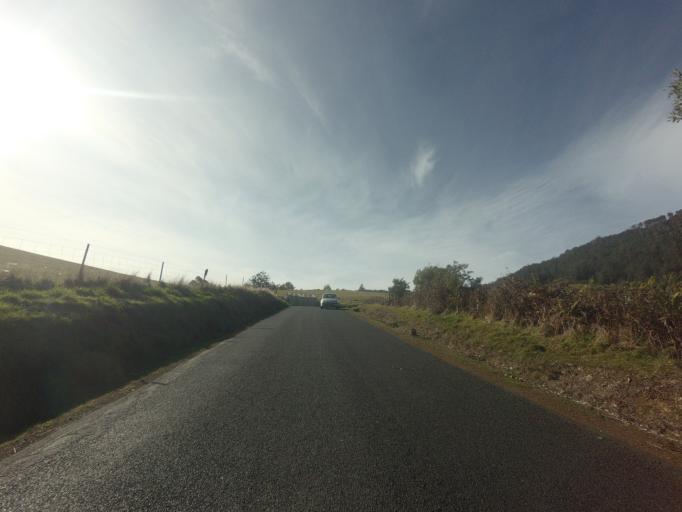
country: AU
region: Tasmania
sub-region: Kingborough
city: Kettering
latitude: -43.1706
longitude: 147.1684
